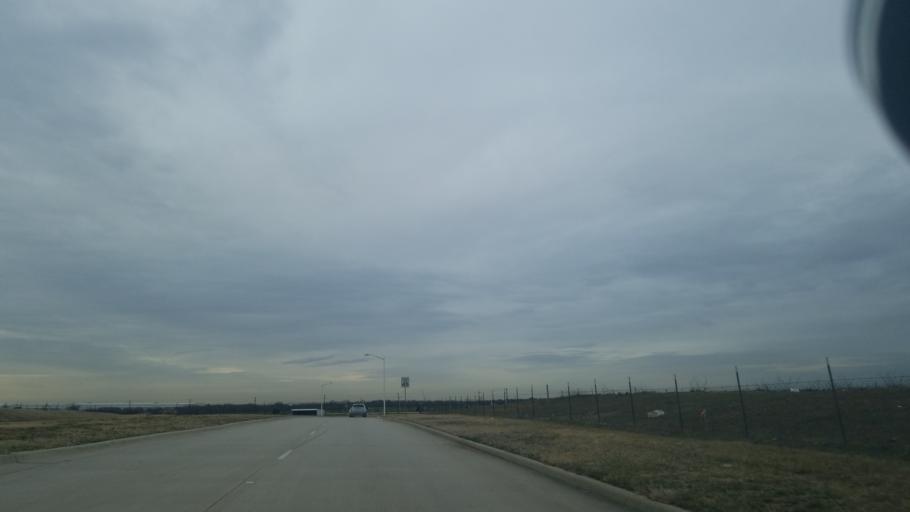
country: US
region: Texas
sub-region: Denton County
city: Denton
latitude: 33.2150
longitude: -97.1852
